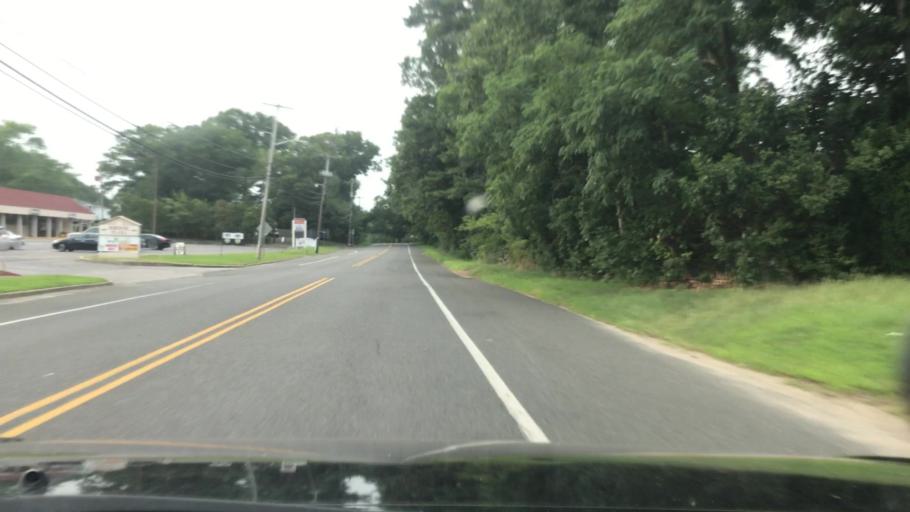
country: US
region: New Jersey
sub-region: Ocean County
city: Lakewood
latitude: 40.1186
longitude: -74.2533
